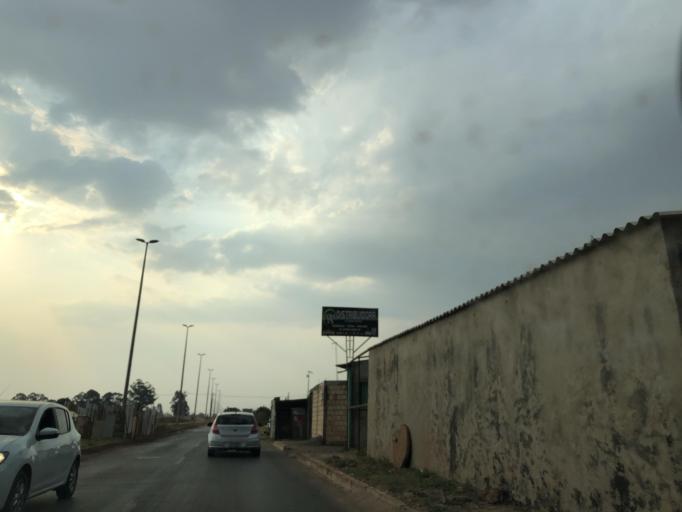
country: BR
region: Federal District
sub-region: Brasilia
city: Brasilia
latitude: -15.9228
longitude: -48.0593
